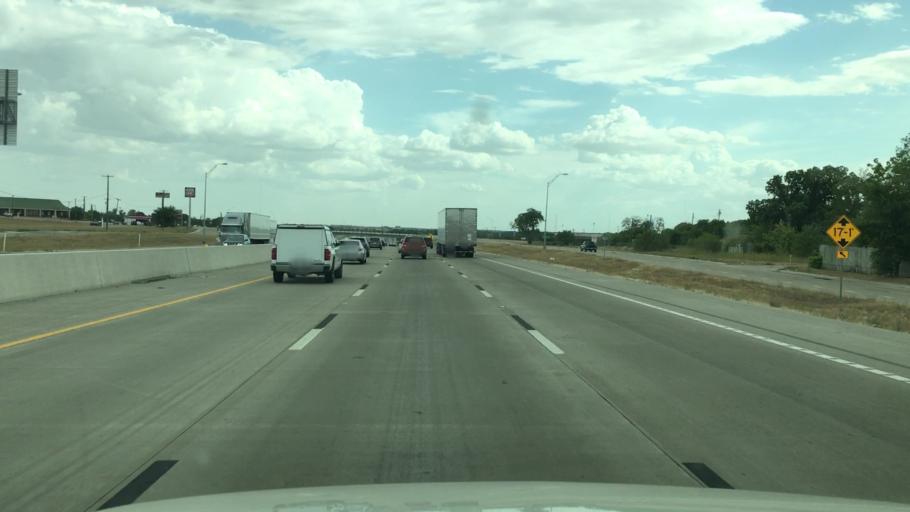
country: US
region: Texas
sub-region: McLennan County
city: Lorena
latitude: 31.3851
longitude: -97.2129
